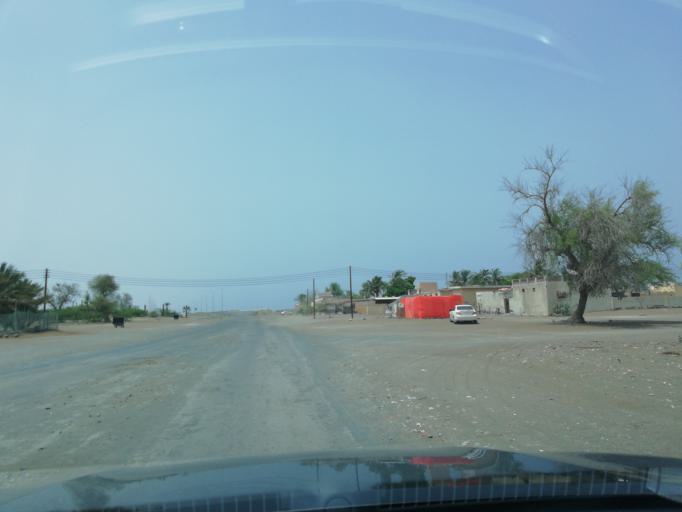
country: OM
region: Al Batinah
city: Al Liwa'
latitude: 24.6186
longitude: 56.5341
